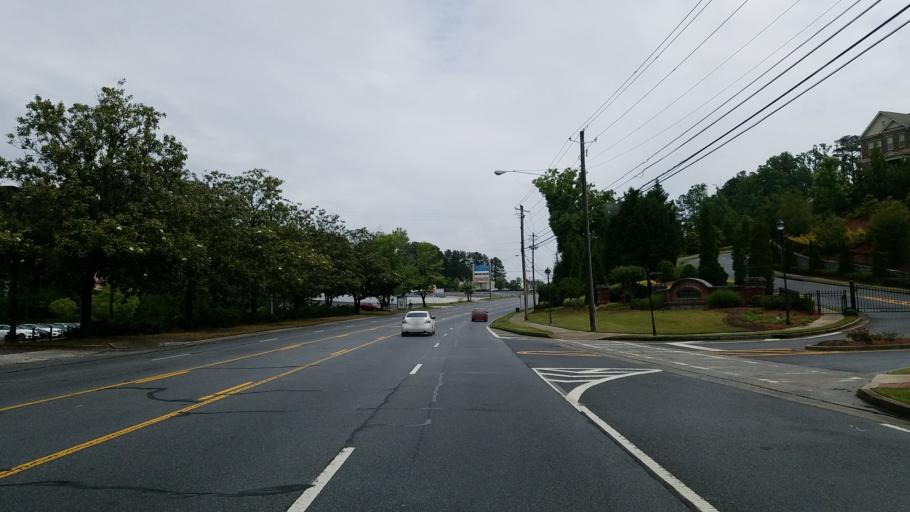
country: US
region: Georgia
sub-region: Fulton County
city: Sandy Springs
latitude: 33.9521
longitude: -84.3673
